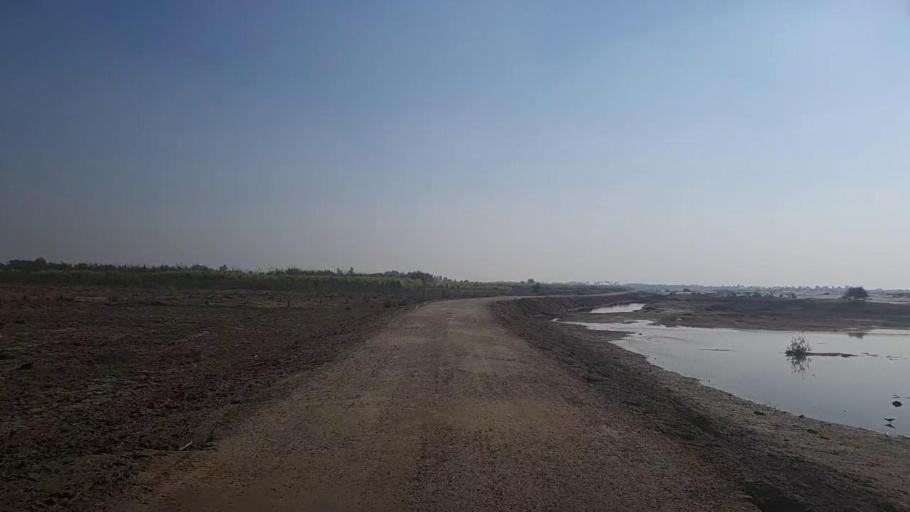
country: PK
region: Sindh
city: Khairpur
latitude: 27.4396
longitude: 68.7277
